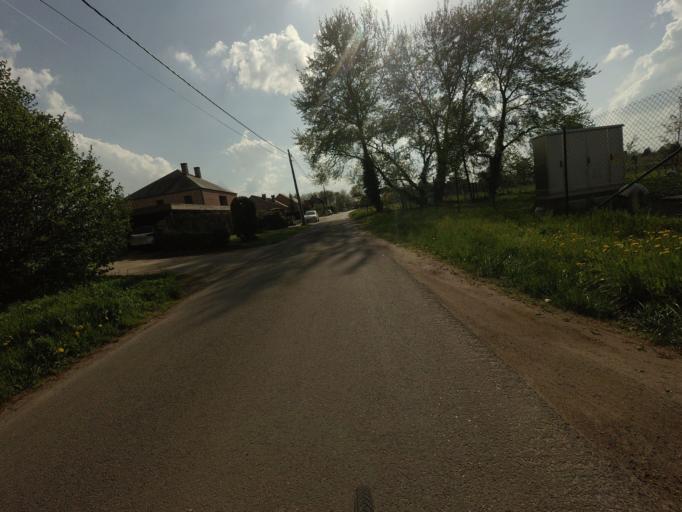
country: BE
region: Flanders
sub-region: Provincie Antwerpen
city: Putte
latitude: 51.0749
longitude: 4.6586
